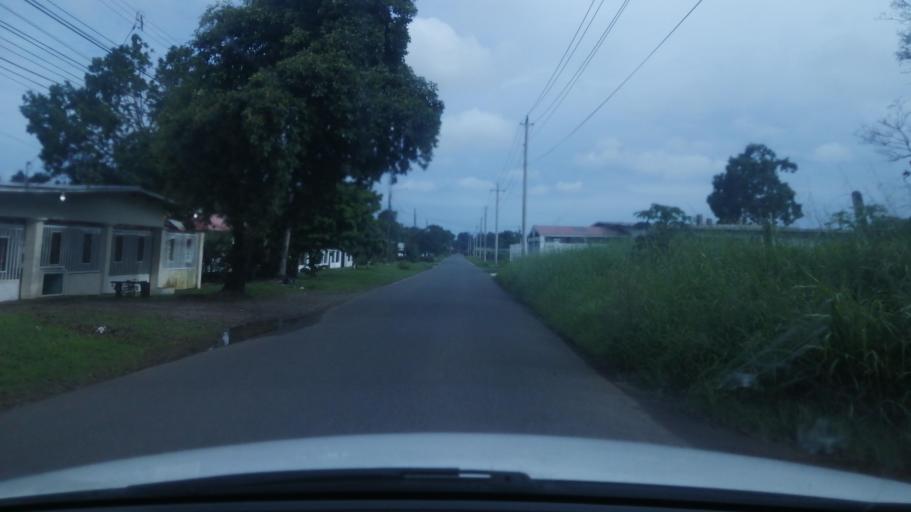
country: PA
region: Chiriqui
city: David
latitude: 8.4078
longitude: -82.4273
